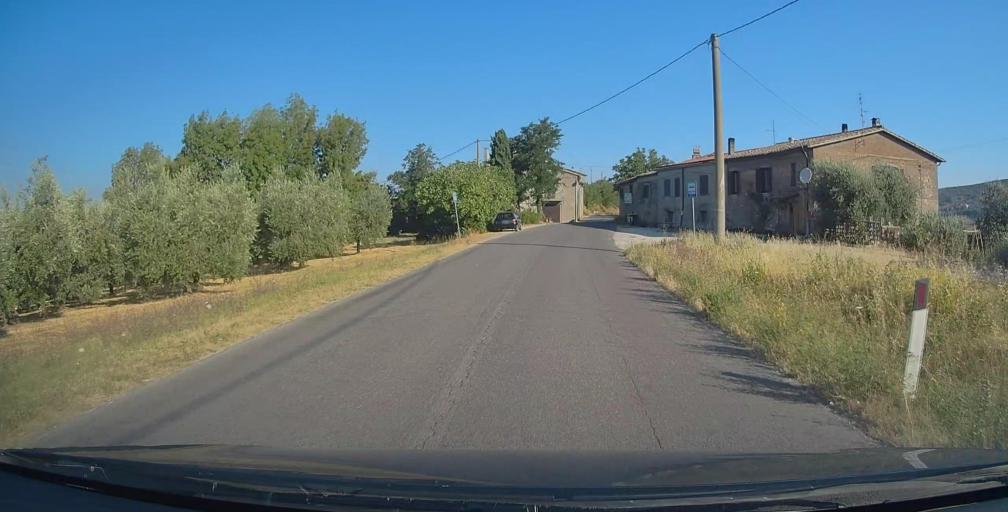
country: IT
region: Umbria
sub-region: Provincia di Terni
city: Calvi dell'Umbria
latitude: 42.4097
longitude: 12.5581
